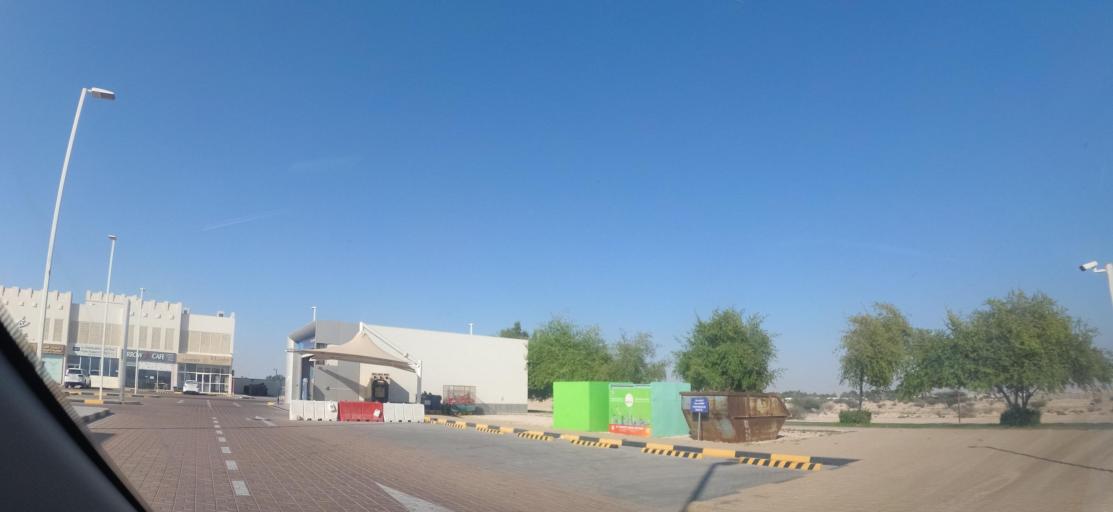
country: QA
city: Al Jumayliyah
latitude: 25.6171
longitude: 51.0861
